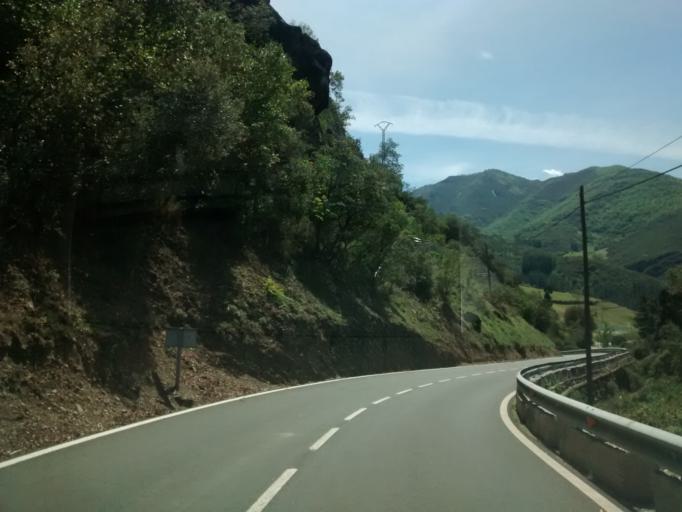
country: ES
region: Cantabria
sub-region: Provincia de Cantabria
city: Potes
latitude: 43.1268
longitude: -4.6289
